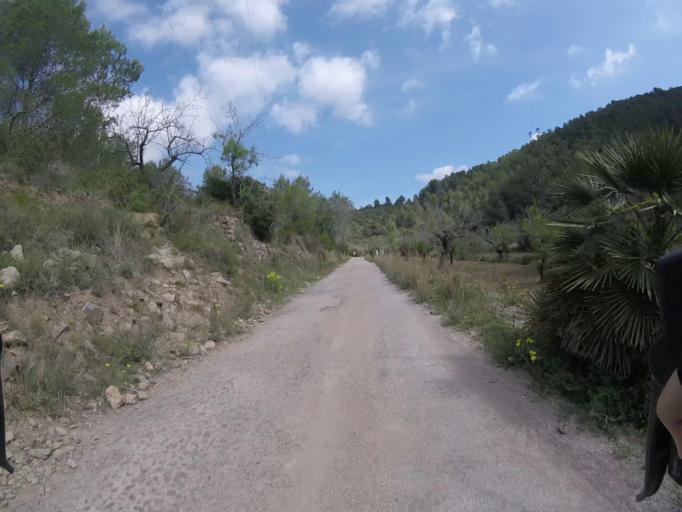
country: ES
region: Valencia
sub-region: Provincia de Castello
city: Cabanes
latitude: 40.1156
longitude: 0.0476
